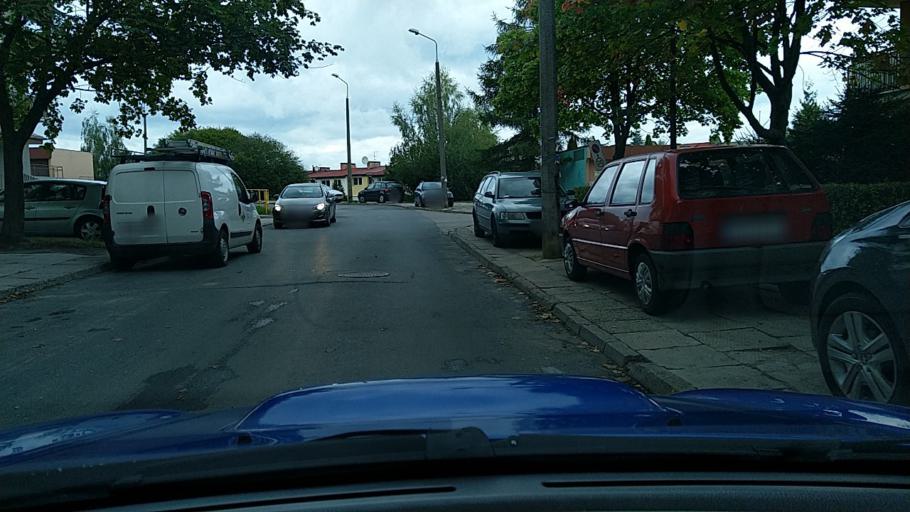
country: PL
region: Warmian-Masurian Voivodeship
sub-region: Olsztyn
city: Kortowo
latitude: 53.7422
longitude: 20.4810
